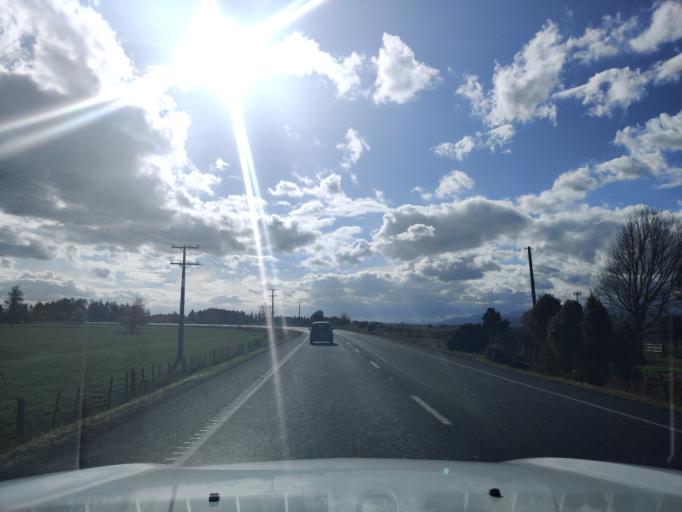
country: NZ
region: Waikato
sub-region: Hauraki District
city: Ngatea
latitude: -37.2751
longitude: 175.5318
